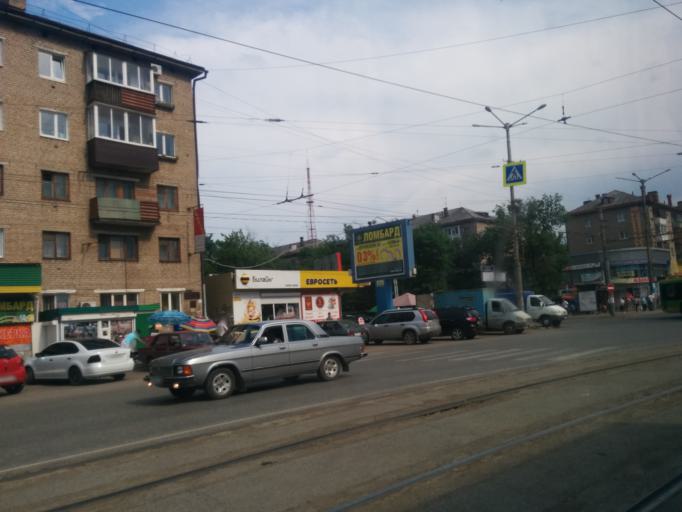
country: RU
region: Perm
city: Perm
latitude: 58.0149
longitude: 56.2811
